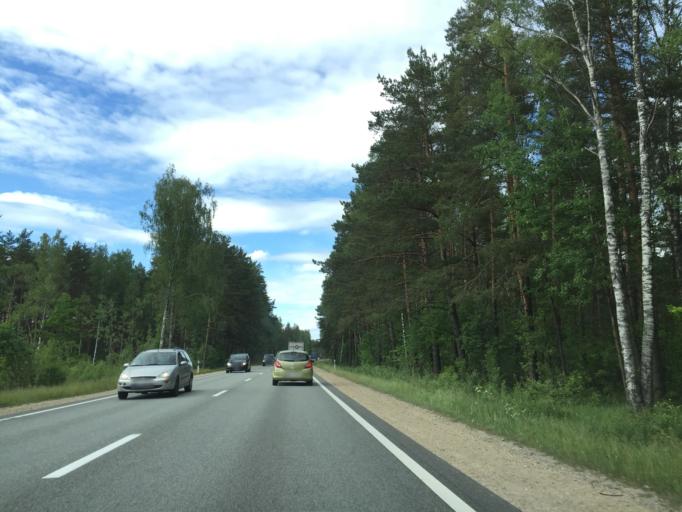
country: LV
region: Riga
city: Bergi
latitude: 56.9530
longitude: 24.3777
